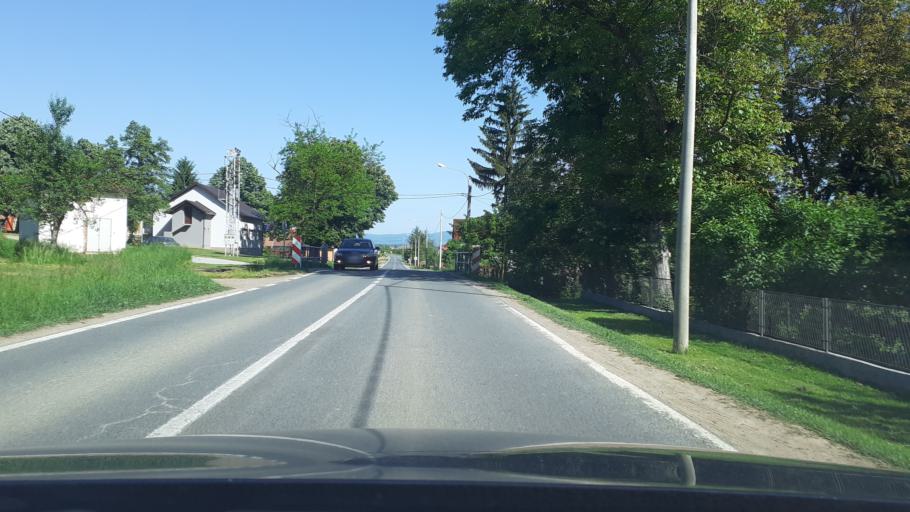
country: HR
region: Pozesko-Slavonska
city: Gradac
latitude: 45.3162
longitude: 17.7756
